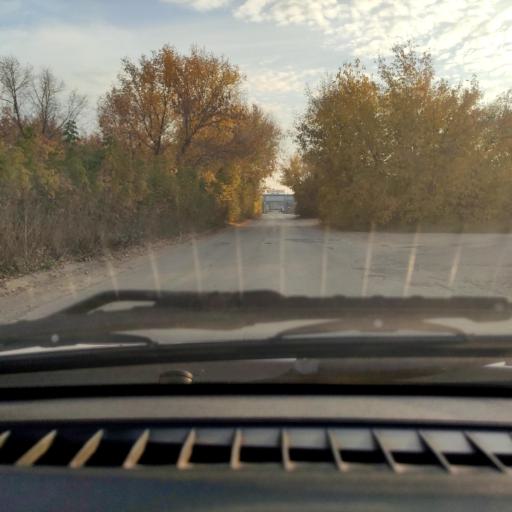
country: RU
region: Samara
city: Tol'yatti
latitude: 53.5276
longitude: 49.4607
